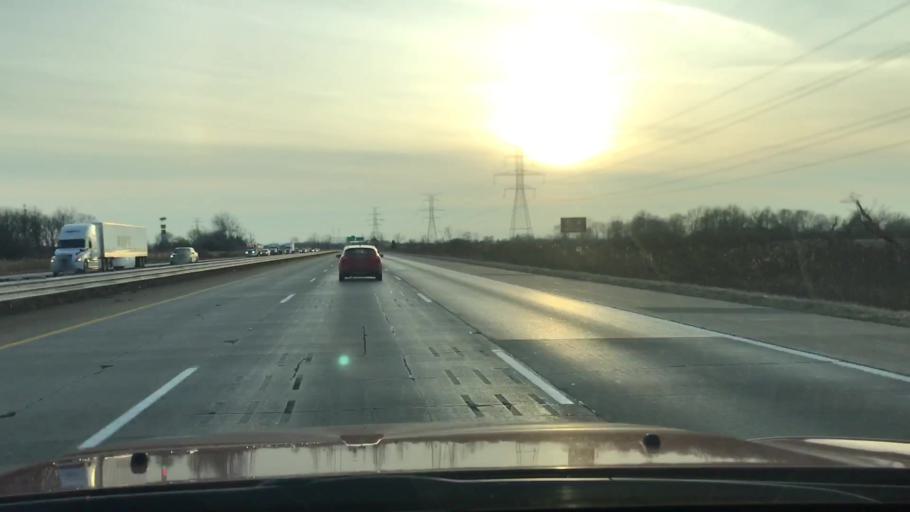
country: US
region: Michigan
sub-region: Monroe County
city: Luna Pier
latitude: 41.8167
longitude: -83.4426
